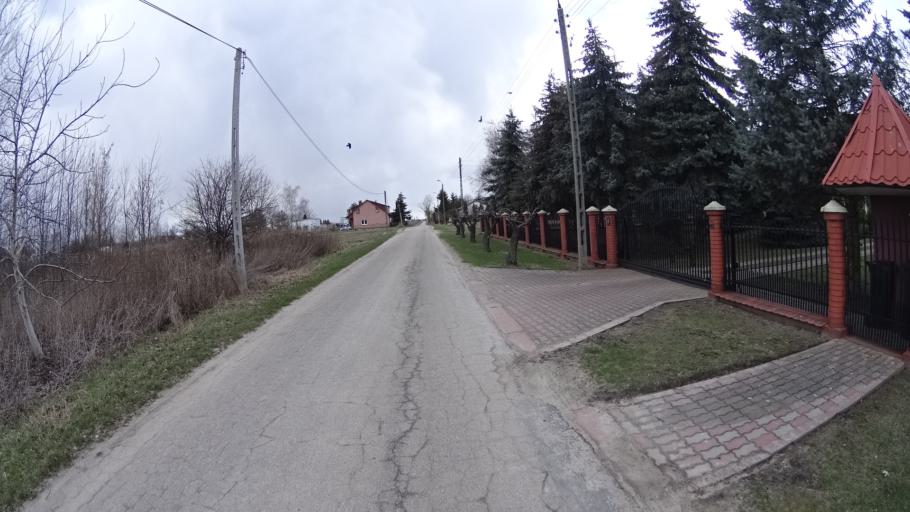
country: PL
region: Masovian Voivodeship
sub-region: Powiat warszawski zachodni
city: Jozefow
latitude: 52.2210
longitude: 20.6865
